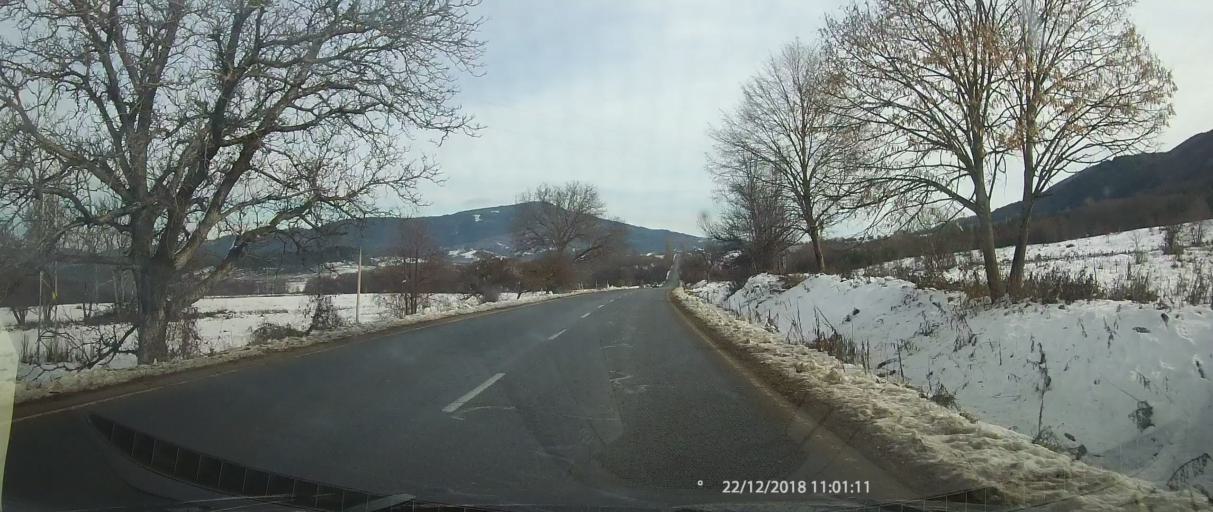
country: BG
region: Kyustendil
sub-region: Obshtina Kyustendil
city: Kyustendil
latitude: 42.2408
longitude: 22.5120
